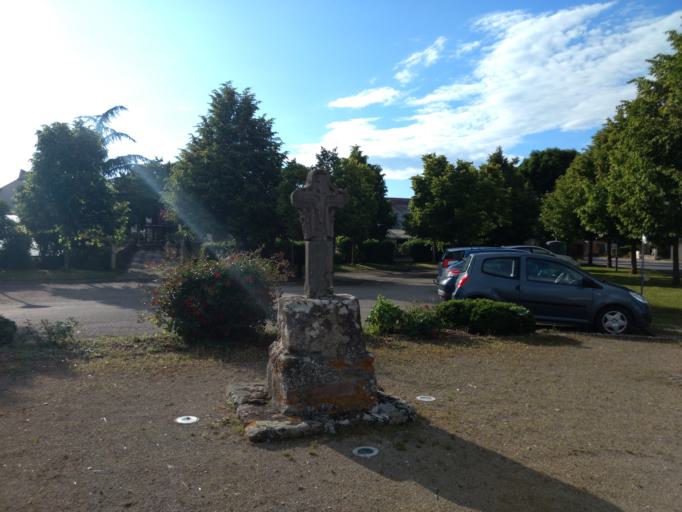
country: FR
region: Midi-Pyrenees
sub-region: Departement de l'Aveyron
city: Olemps
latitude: 44.3467
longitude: 2.5531
